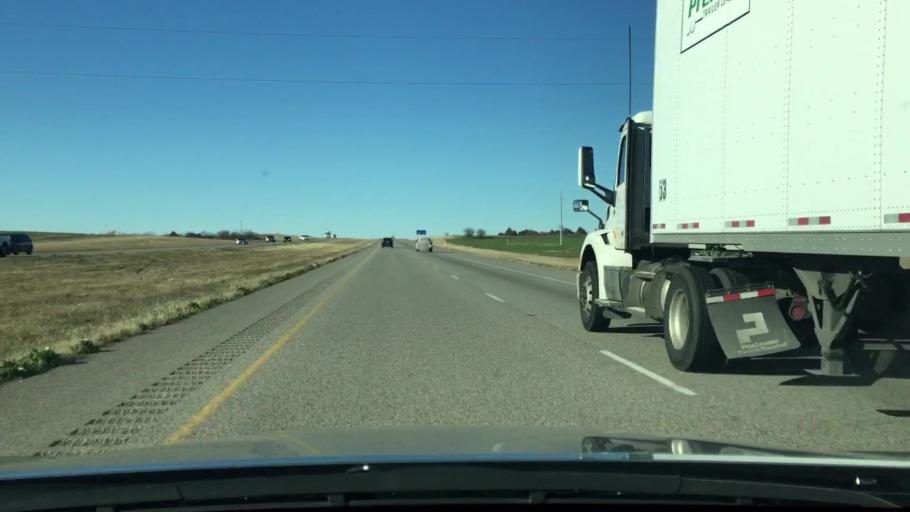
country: US
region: Texas
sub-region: Hill County
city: Itasca
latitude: 32.1363
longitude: -97.1209
